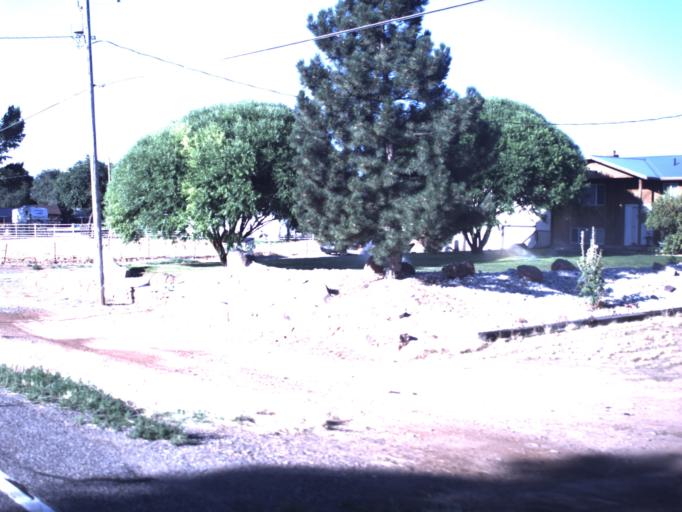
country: US
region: Utah
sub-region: Sevier County
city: Aurora
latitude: 38.8631
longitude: -111.9655
